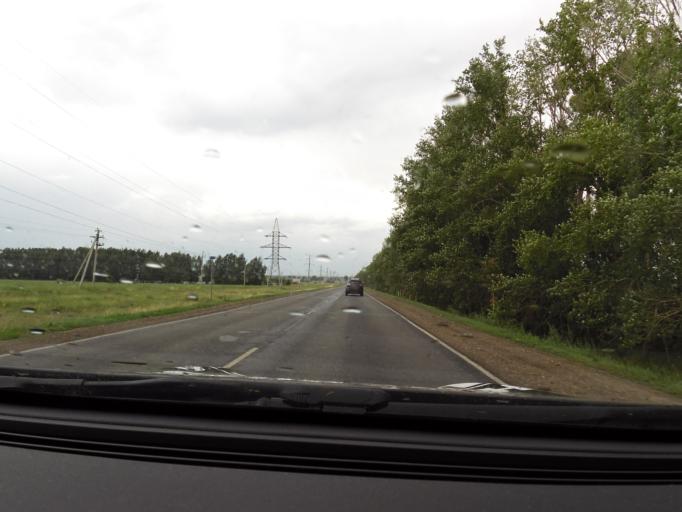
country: RU
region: Bashkortostan
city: Mikhaylovka
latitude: 54.8595
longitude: 55.7581
